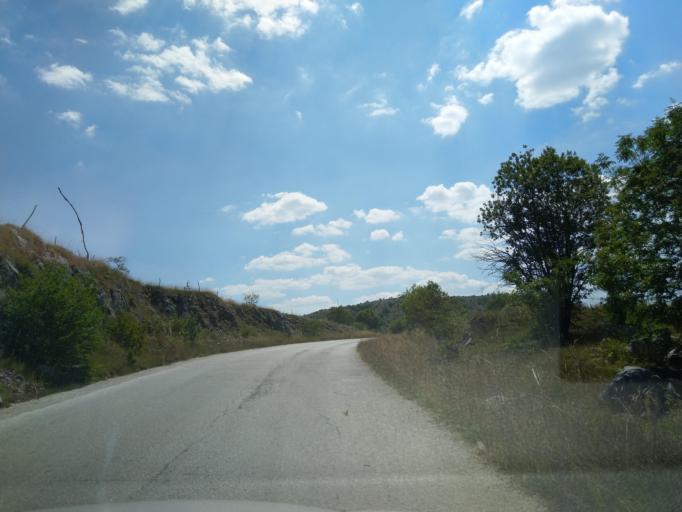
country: RS
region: Central Serbia
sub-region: Zlatiborski Okrug
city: Nova Varos
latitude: 43.4311
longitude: 19.9499
